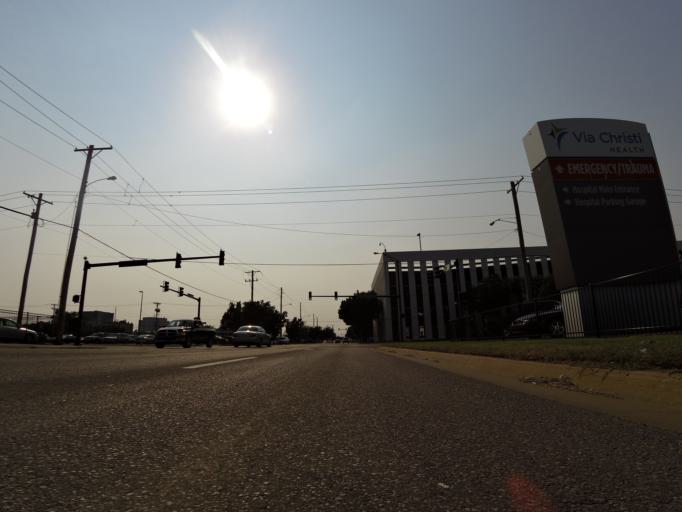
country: US
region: Kansas
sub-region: Sedgwick County
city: Wichita
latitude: 37.6976
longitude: -97.3312
